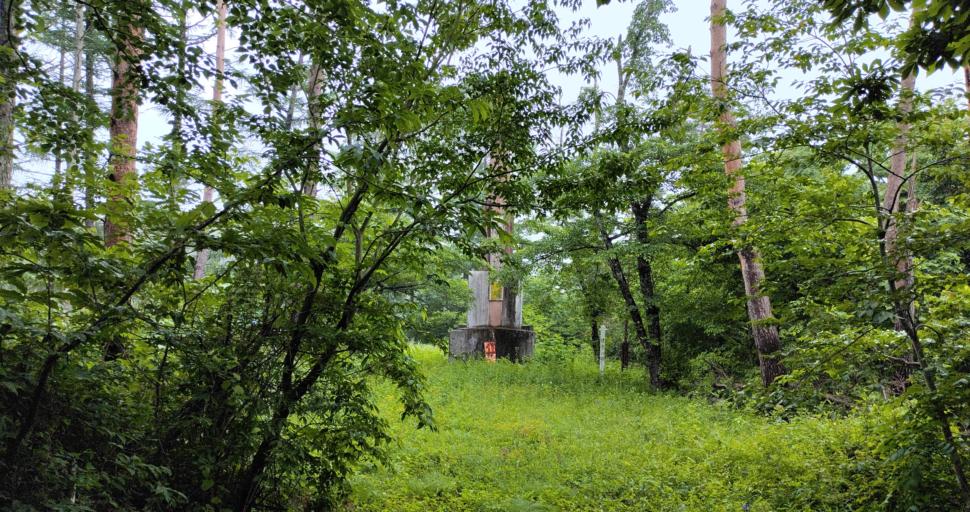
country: JP
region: Nagano
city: Komoro
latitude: 36.2830
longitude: 138.3703
